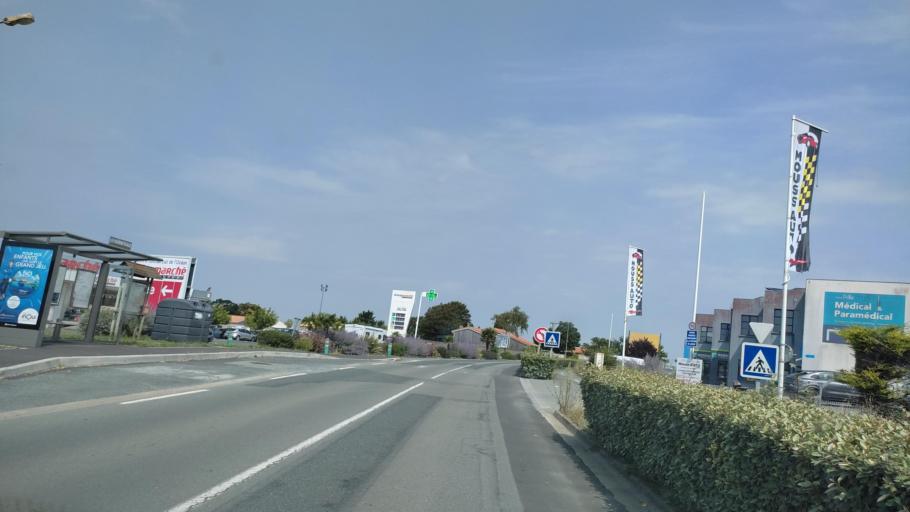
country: FR
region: Poitou-Charentes
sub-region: Departement de la Charente-Maritime
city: Chatelaillon-Plage
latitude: 46.0834
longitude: -1.0742
